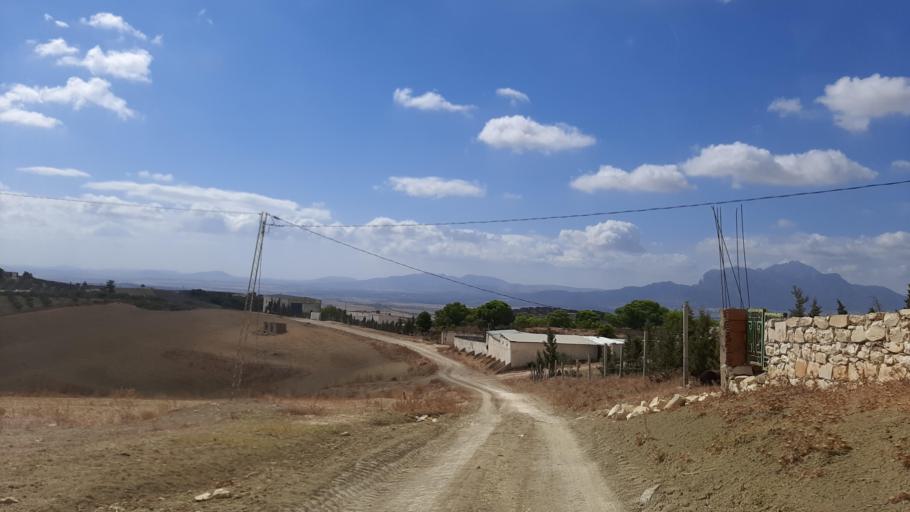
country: TN
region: Zaghwan
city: Zaghouan
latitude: 36.4902
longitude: 10.1773
